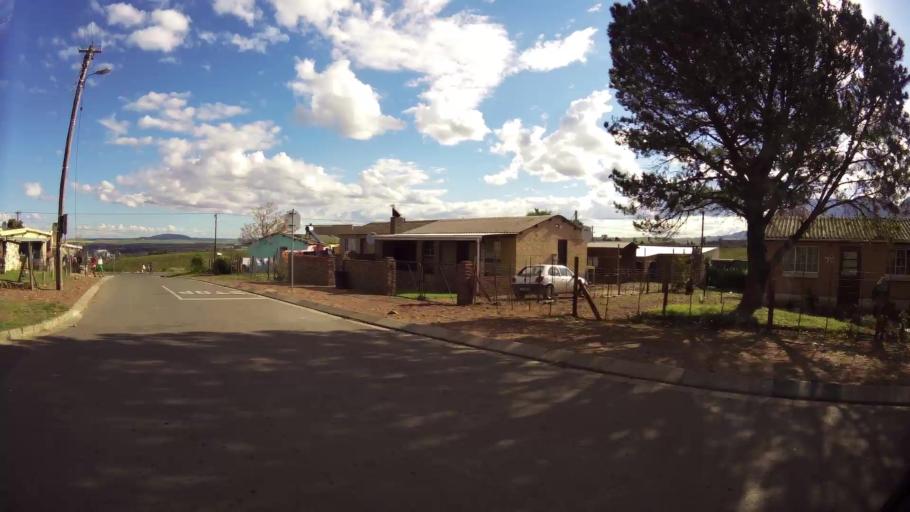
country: ZA
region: Western Cape
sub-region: Overberg District Municipality
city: Swellendam
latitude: -34.0395
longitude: 20.4400
